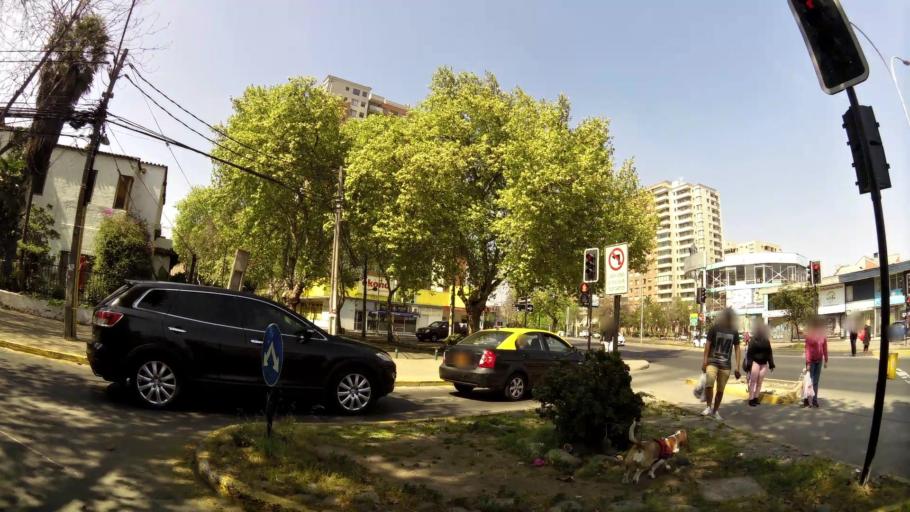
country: CL
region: Santiago Metropolitan
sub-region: Provincia de Santiago
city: Santiago
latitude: -33.4533
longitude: -70.6231
